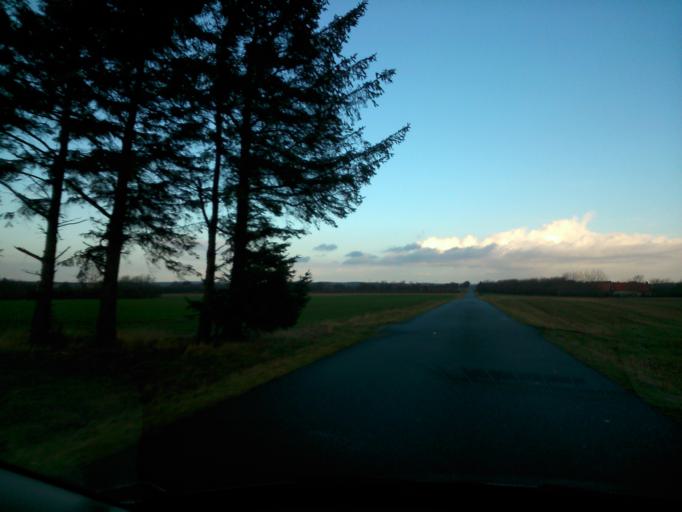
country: DK
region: Central Jutland
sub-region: Ringkobing-Skjern Kommune
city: Videbaek
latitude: 56.0444
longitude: 8.5692
